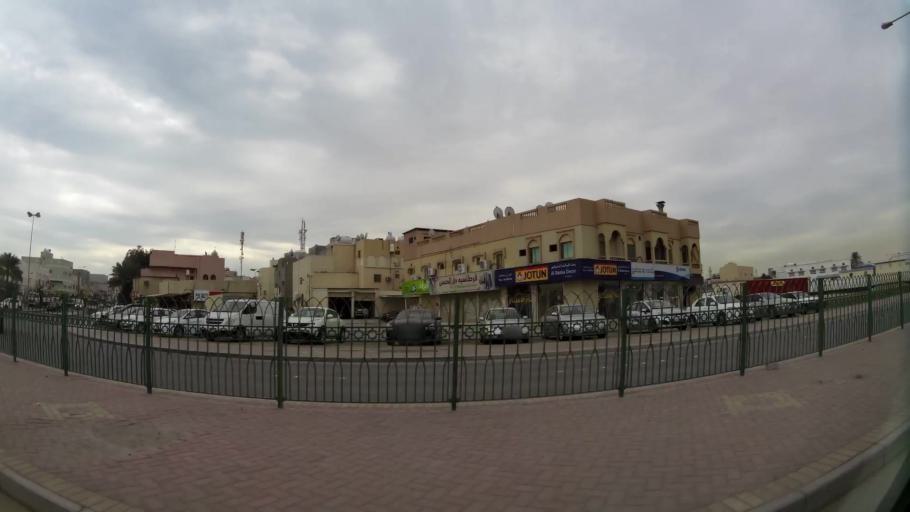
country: BH
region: Northern
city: Sitrah
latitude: 26.1653
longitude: 50.6136
